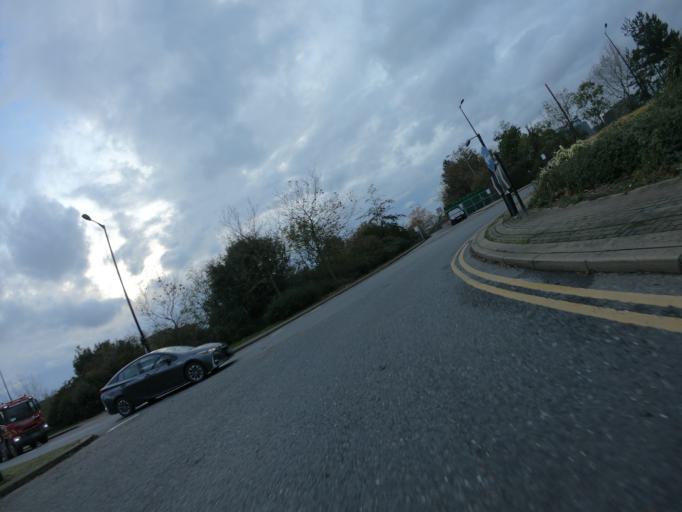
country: GB
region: England
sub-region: Greater London
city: Woolwich
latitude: 51.5045
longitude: 0.0396
